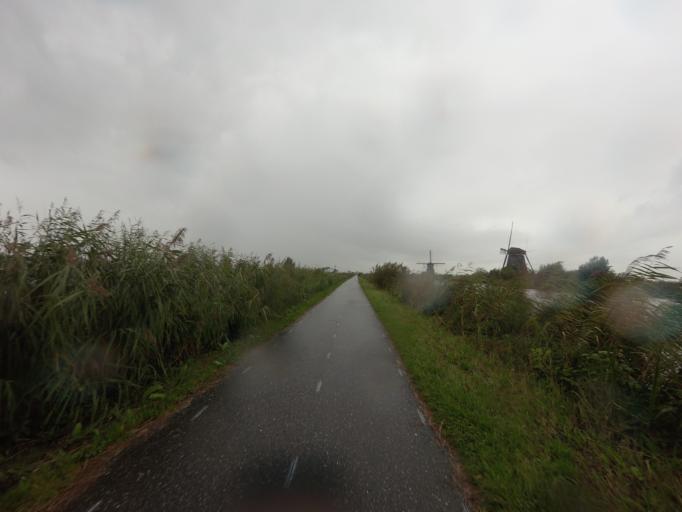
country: NL
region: South Holland
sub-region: Gemeente Alblasserdam
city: Alblasserdam
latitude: 51.8766
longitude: 4.6579
